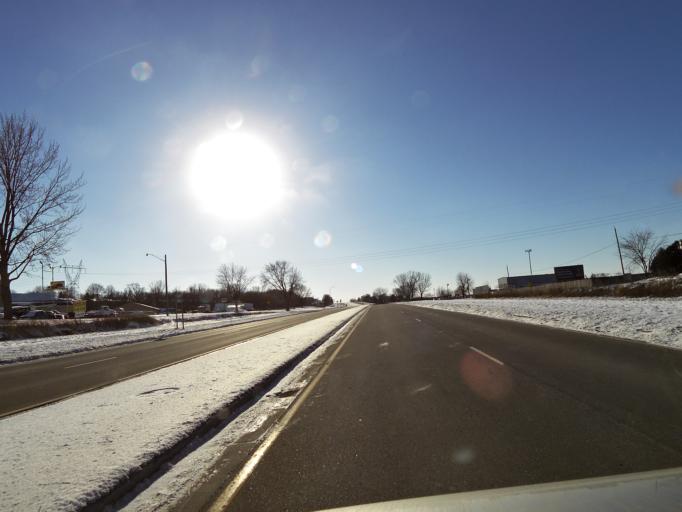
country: US
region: Minnesota
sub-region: Scott County
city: Shakopee
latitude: 44.7935
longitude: -93.5468
